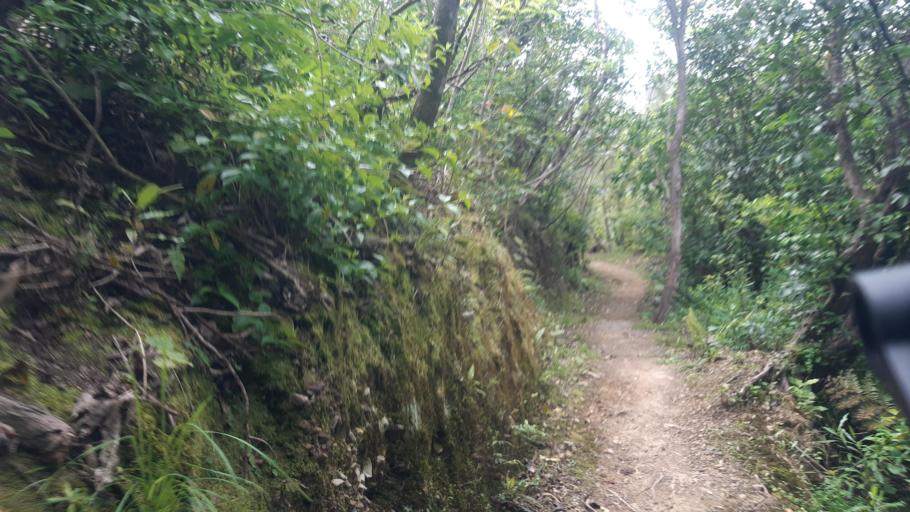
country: NZ
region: Marlborough
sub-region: Marlborough District
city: Picton
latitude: -41.2850
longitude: 174.0131
